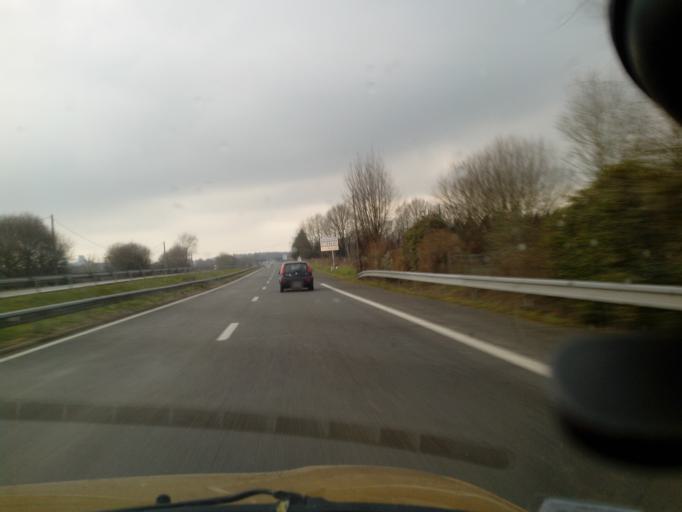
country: FR
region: Brittany
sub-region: Departement du Morbihan
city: Reguiny
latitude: 47.9210
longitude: -2.7117
